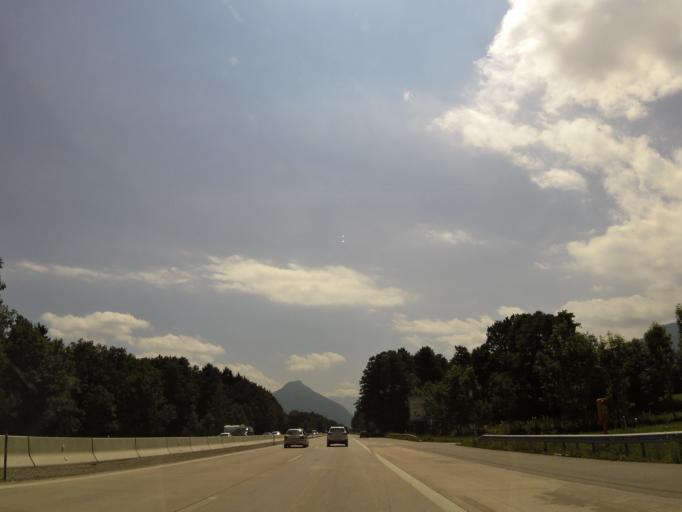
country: DE
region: Bavaria
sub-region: Upper Bavaria
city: Brannenburg
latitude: 47.7598
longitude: 12.1075
